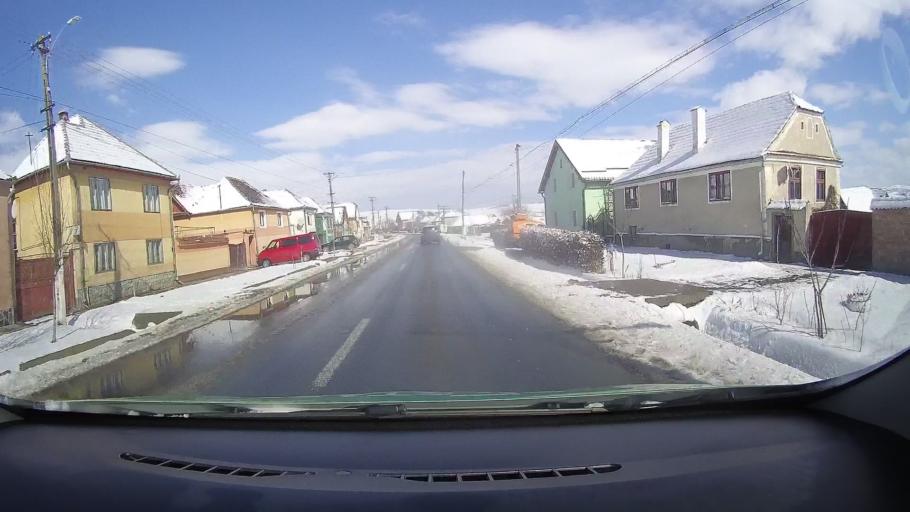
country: RO
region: Sibiu
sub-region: Comuna Nocrich
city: Nocrich
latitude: 45.8985
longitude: 24.4577
